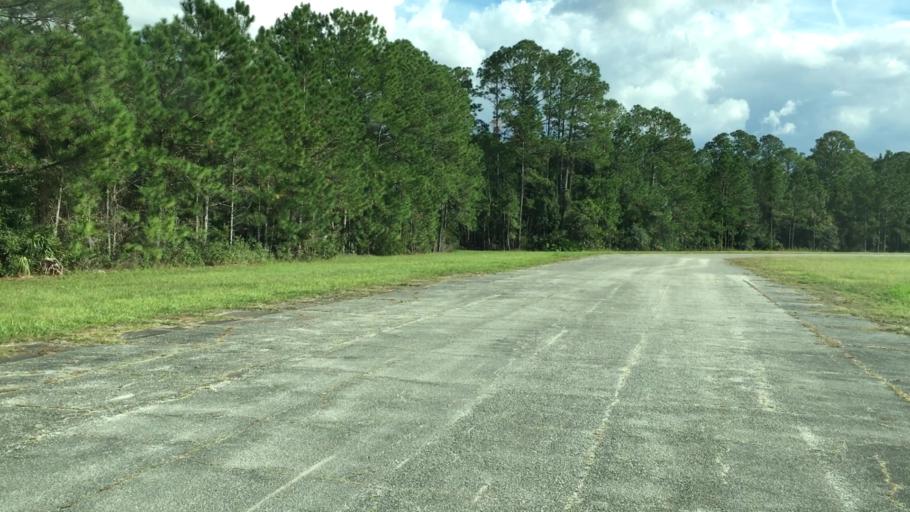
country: US
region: Florida
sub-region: Volusia County
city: North DeLand
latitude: 29.0763
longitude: -81.2859
